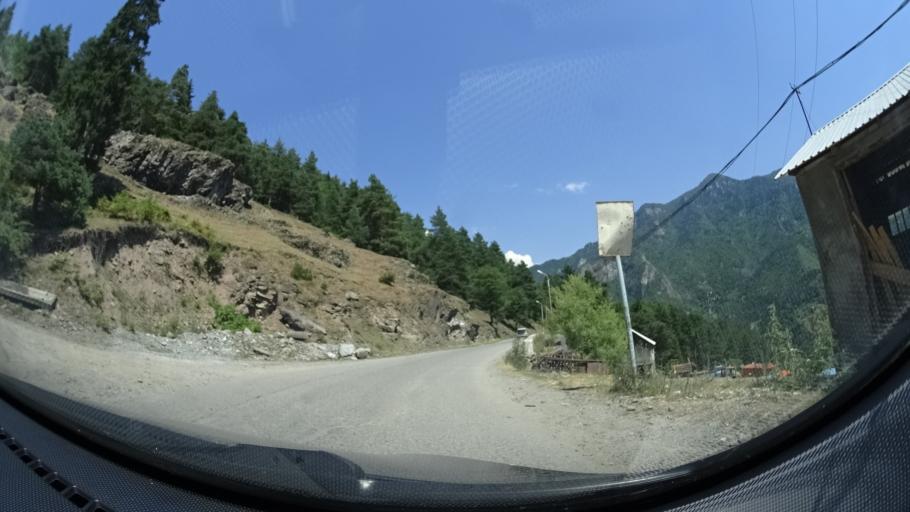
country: GE
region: Ajaria
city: Khulo
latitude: 41.6397
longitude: 42.3052
